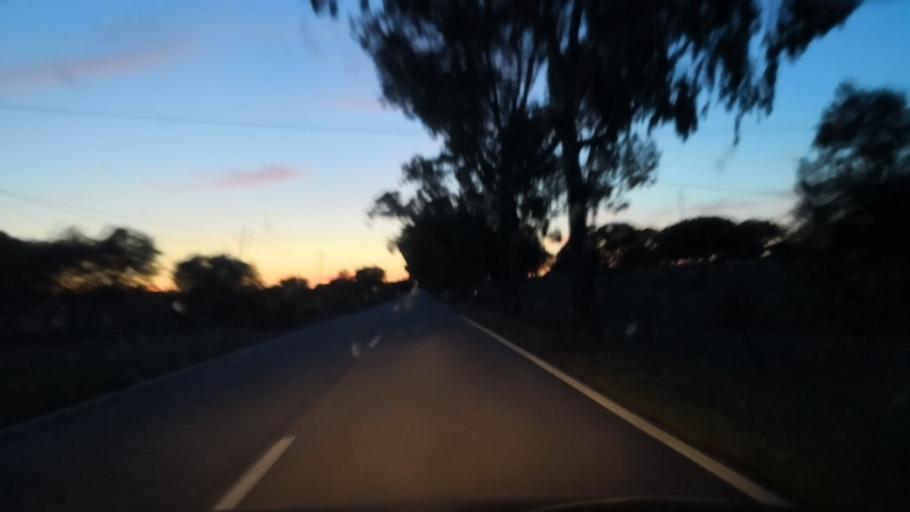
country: ES
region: Extremadura
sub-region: Provincia de Caceres
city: Piedras Albas
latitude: 39.8629
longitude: -7.0093
